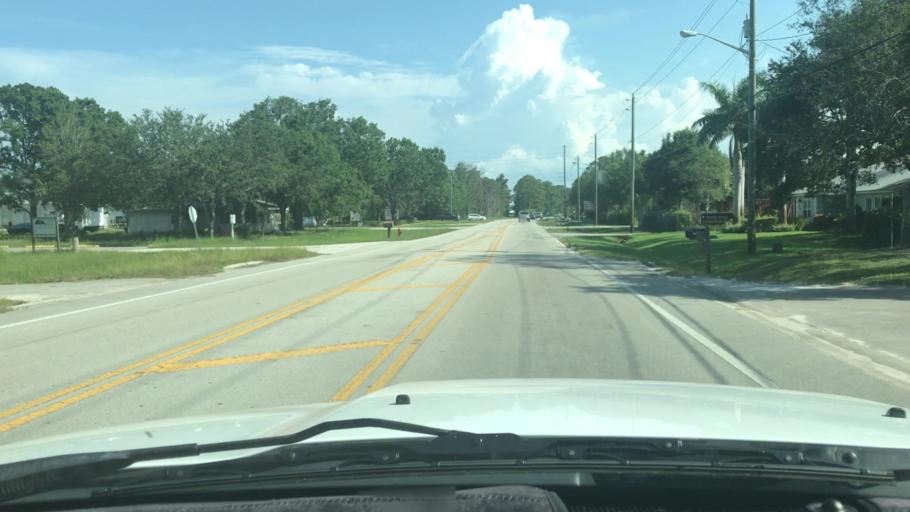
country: US
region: Florida
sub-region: Indian River County
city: Gifford
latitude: 27.6659
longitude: -80.4298
